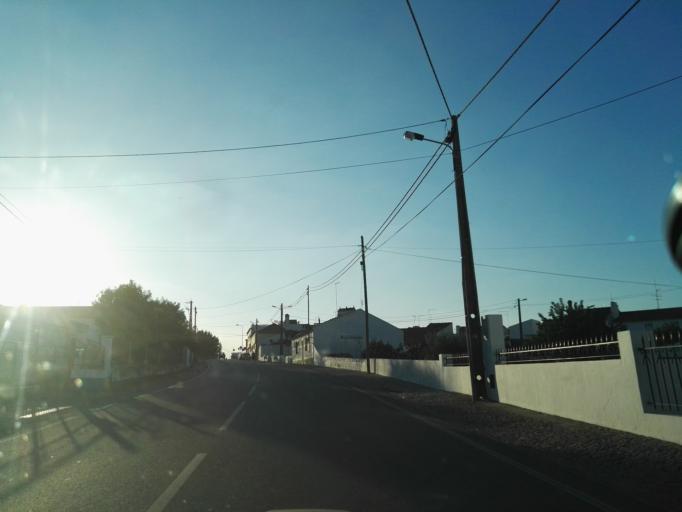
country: PT
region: Evora
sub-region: Arraiolos
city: Arraiolos
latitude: 38.8299
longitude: -7.8373
